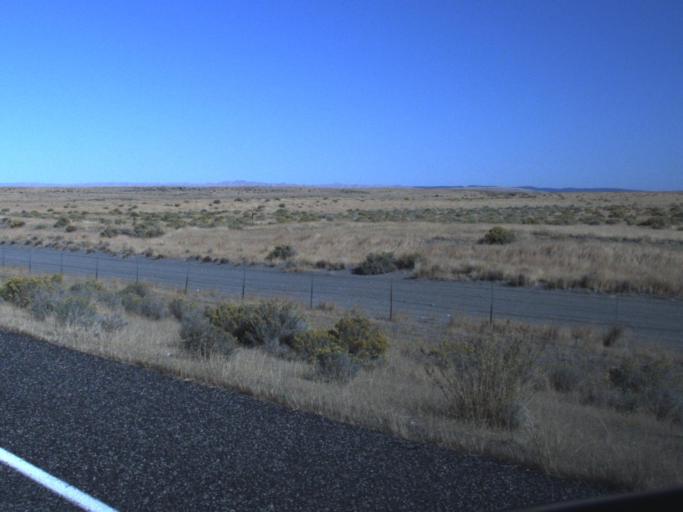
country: US
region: Washington
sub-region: Benton County
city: Benton City
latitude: 46.4399
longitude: -119.4890
